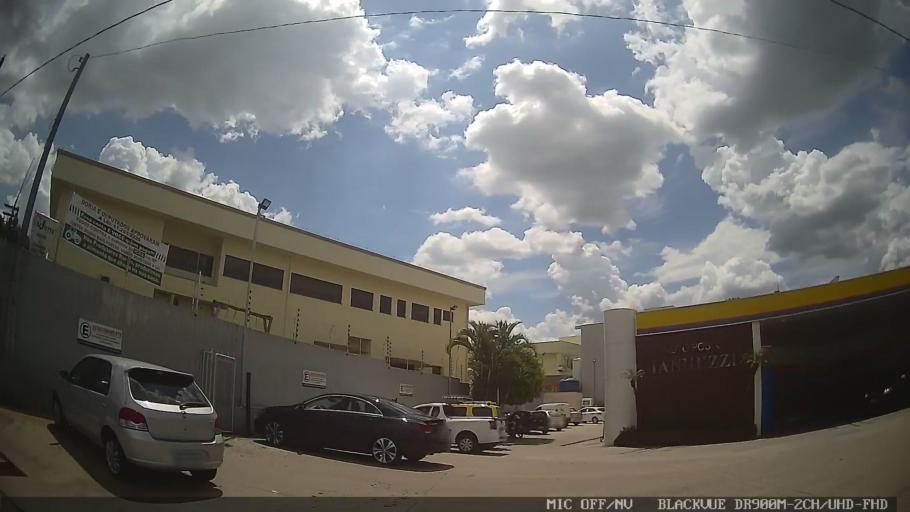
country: BR
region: Sao Paulo
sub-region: Atibaia
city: Atibaia
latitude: -23.1172
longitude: -46.5617
